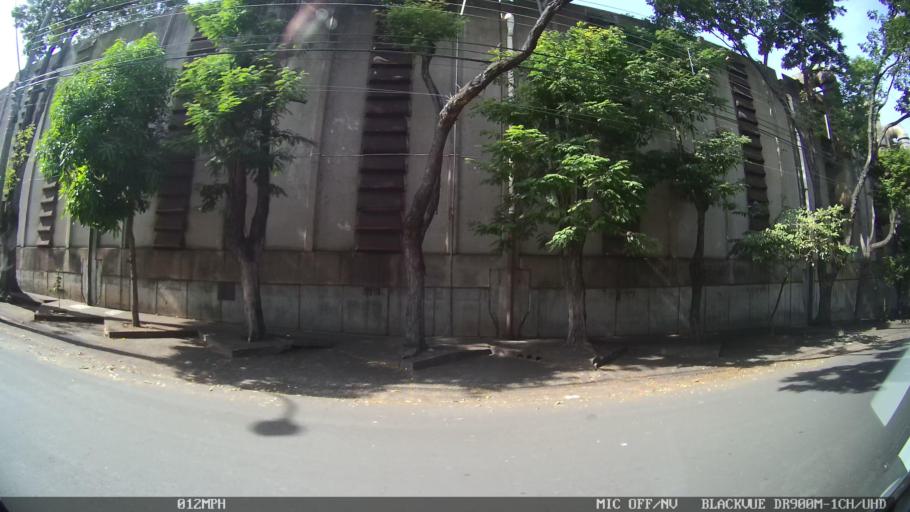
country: BR
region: Sao Paulo
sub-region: Piracicaba
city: Piracicaba
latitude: -22.7064
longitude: -47.6570
